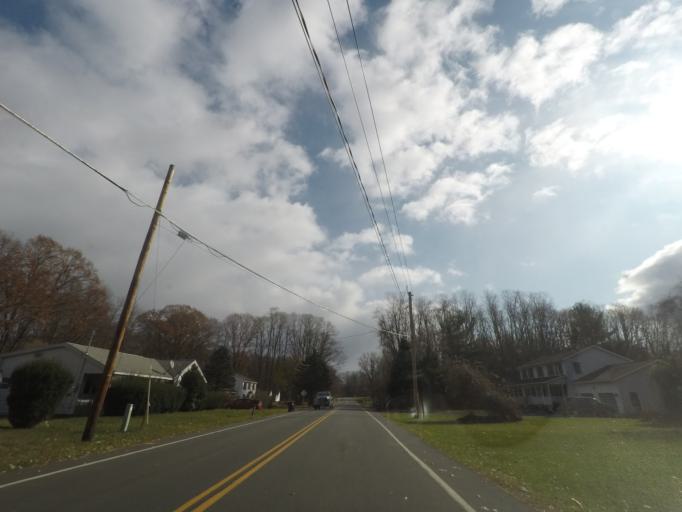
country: US
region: New York
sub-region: Saratoga County
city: Country Knolls
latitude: 42.9153
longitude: -73.8302
